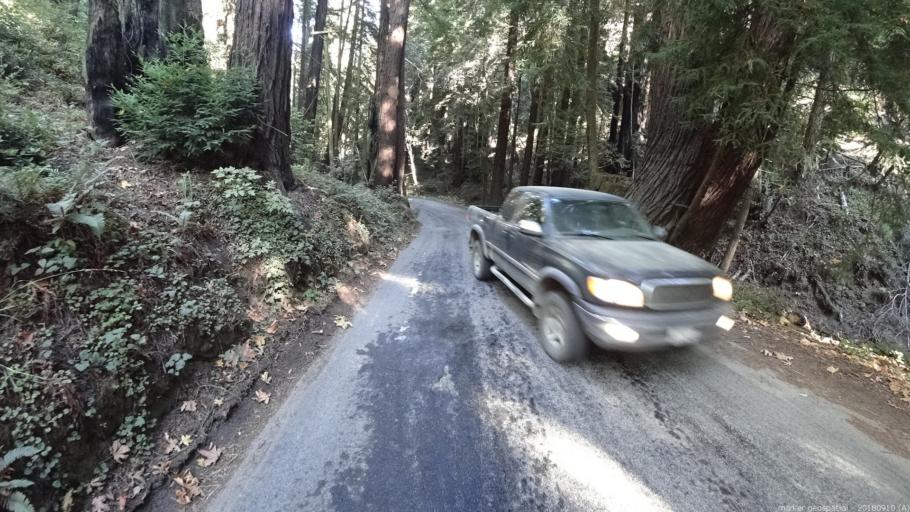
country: US
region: California
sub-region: Monterey County
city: Carmel Valley Village
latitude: 36.3977
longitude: -121.8851
